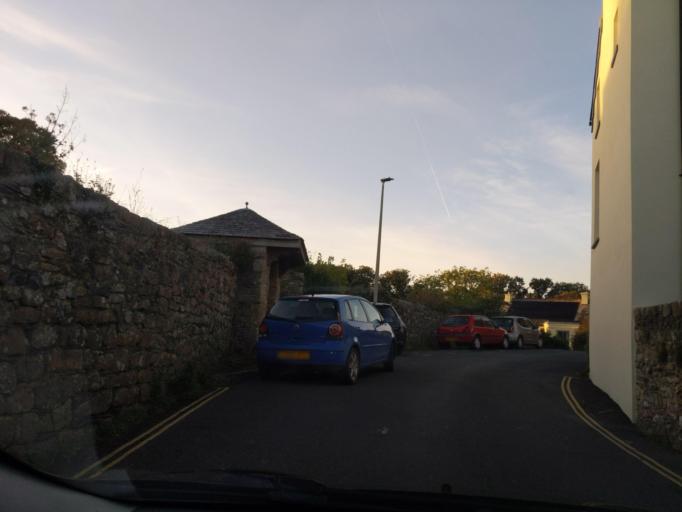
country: GB
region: England
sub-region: Devon
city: South Brent
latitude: 50.4277
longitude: -3.8364
